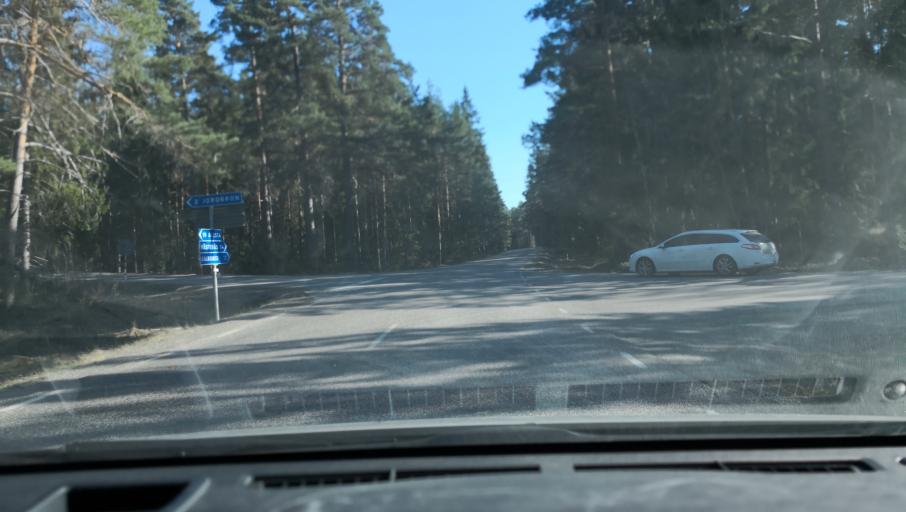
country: SE
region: Dalarna
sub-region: Avesta Kommun
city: Avesta
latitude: 60.0225
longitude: 16.3360
